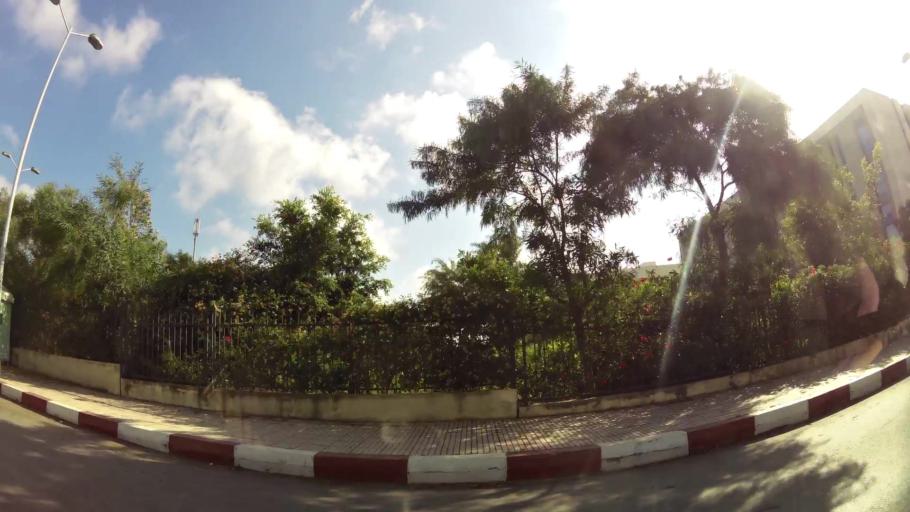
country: MA
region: Rabat-Sale-Zemmour-Zaer
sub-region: Skhirate-Temara
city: Temara
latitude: 33.9536
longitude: -6.8718
